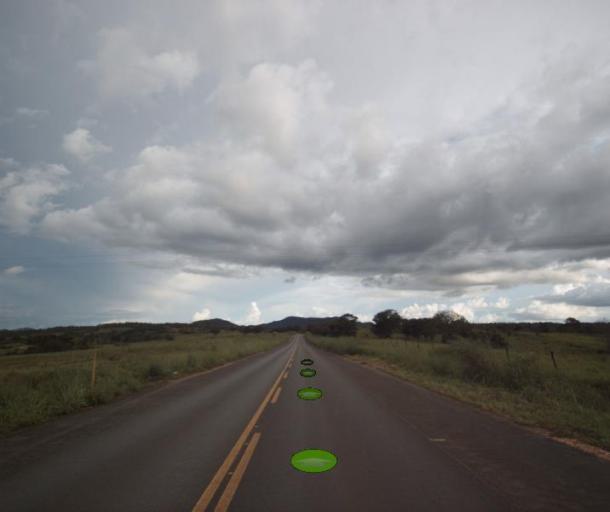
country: BR
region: Goias
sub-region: Niquelandia
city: Niquelandia
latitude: -14.4822
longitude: -48.4889
